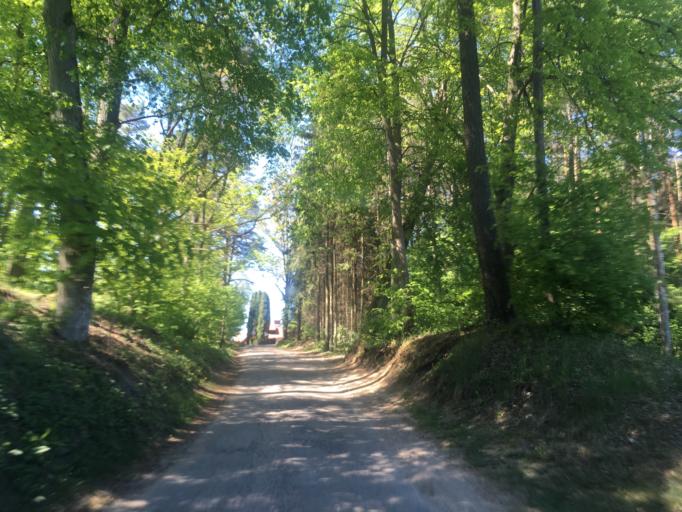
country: PL
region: Warmian-Masurian Voivodeship
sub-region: Powiat mragowski
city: Mikolajki
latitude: 53.7543
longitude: 21.6104
